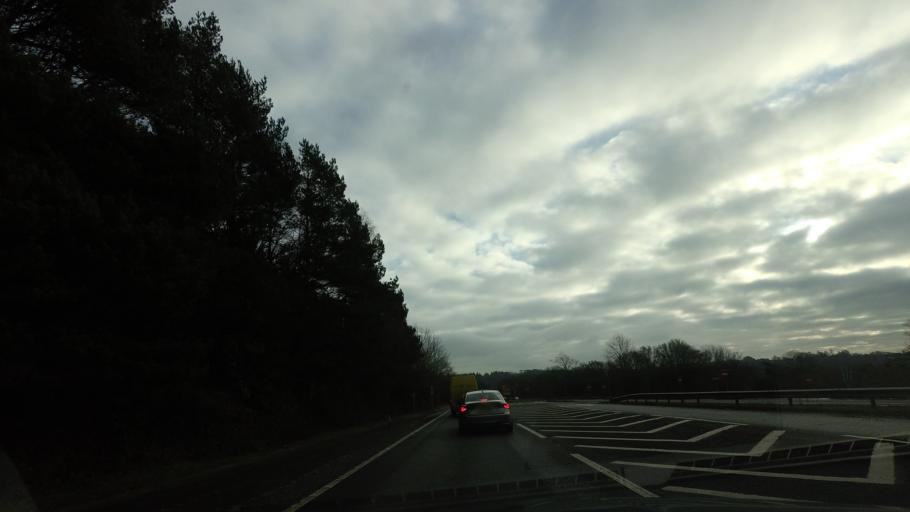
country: GB
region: England
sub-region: Kent
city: Hawkhurst
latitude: 51.0630
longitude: 0.4422
